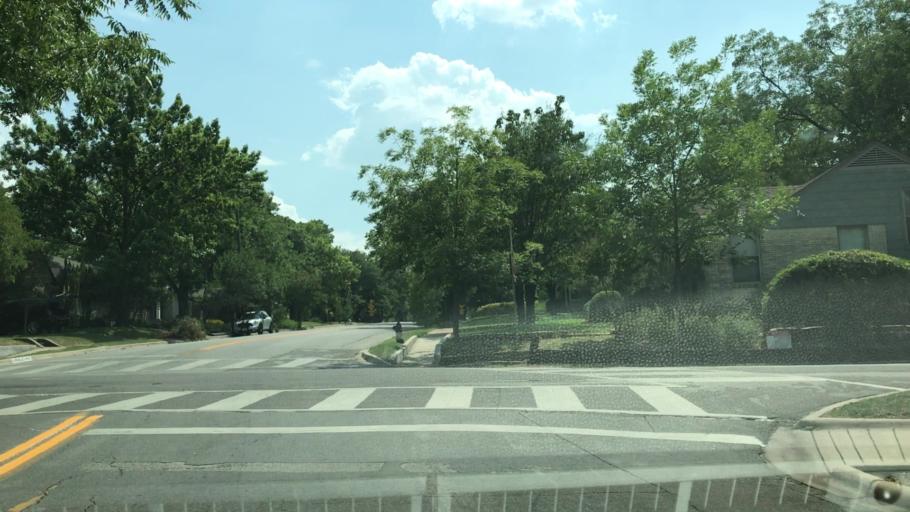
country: US
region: Texas
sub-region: Dallas County
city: Highland Park
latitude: 32.8077
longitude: -96.7387
